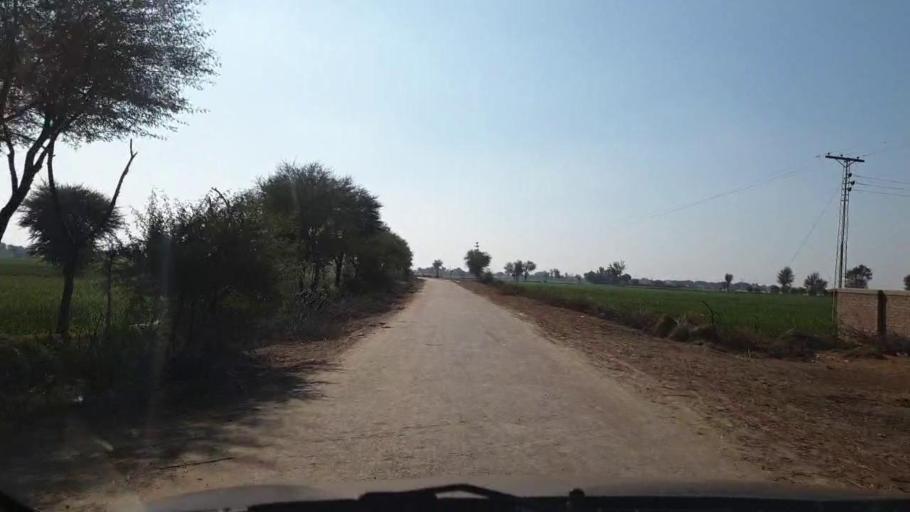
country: PK
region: Sindh
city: Sinjhoro
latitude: 25.9529
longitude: 68.7447
